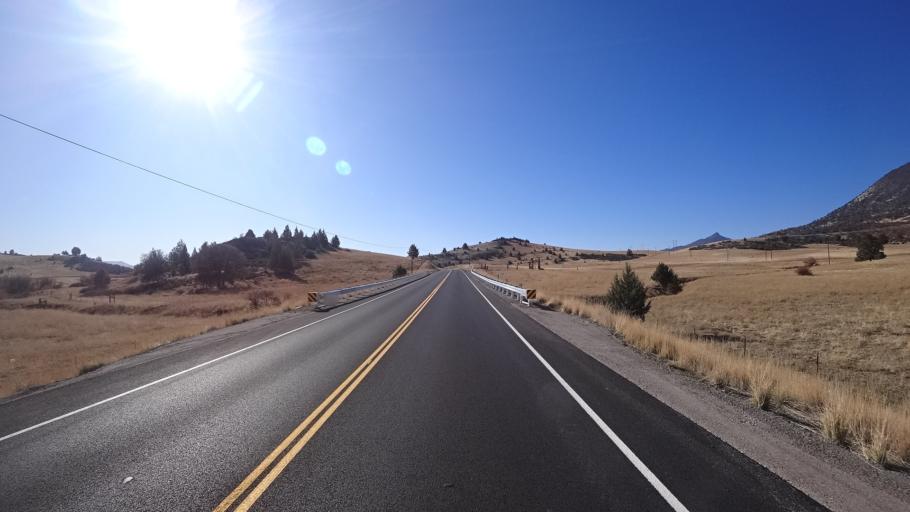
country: US
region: California
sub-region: Siskiyou County
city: Montague
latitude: 41.8586
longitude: -122.4650
